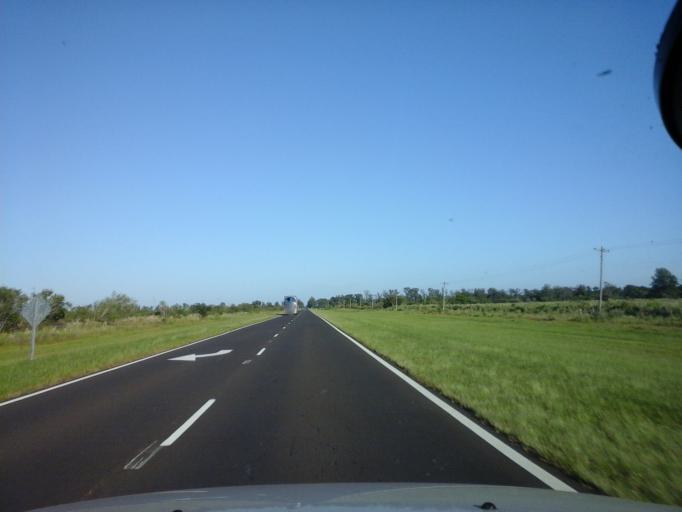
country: AR
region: Corrientes
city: Ita Ibate
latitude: -27.4664
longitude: -57.3087
